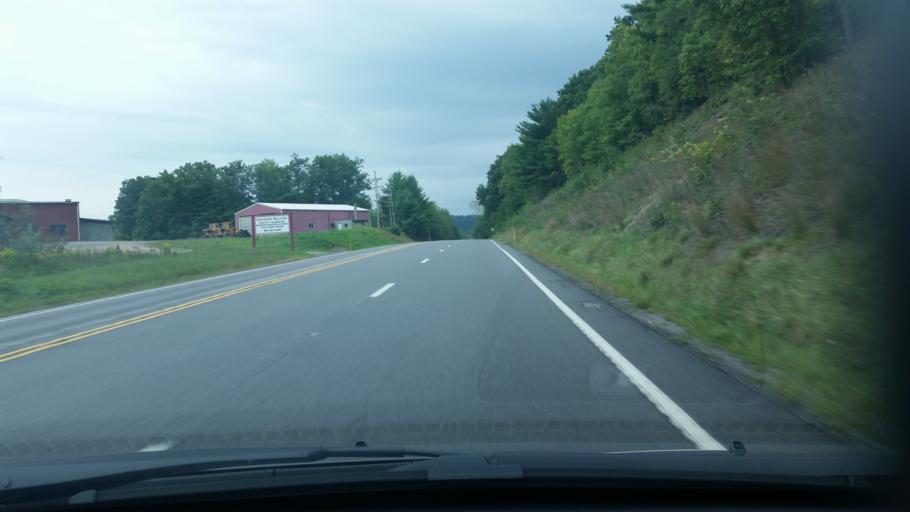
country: US
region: Pennsylvania
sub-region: Clearfield County
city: Shiloh
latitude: 41.0719
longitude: -78.3089
